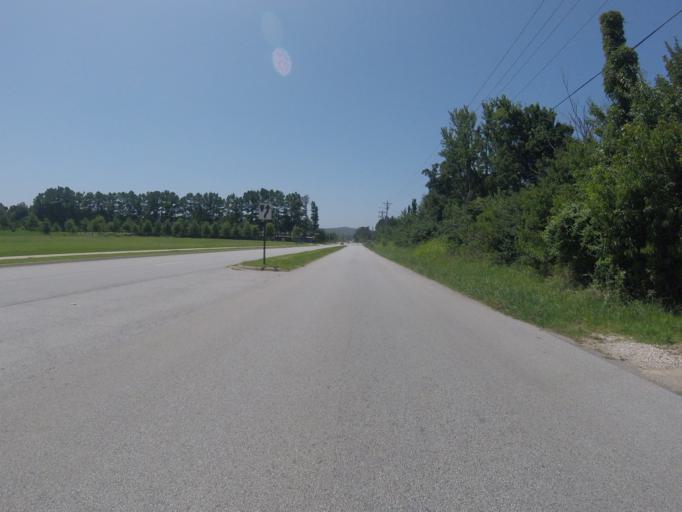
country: US
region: Arkansas
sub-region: Washington County
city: Farmington
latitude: 36.0815
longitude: -94.2175
